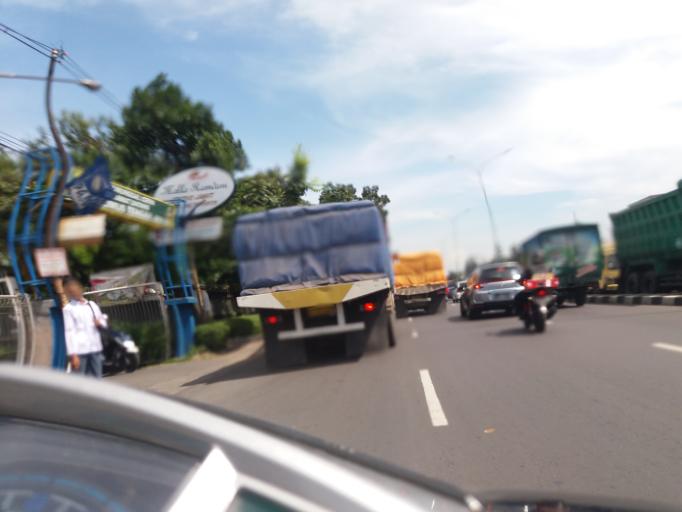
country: ID
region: West Java
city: Bandung
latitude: -6.9466
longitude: 107.6381
